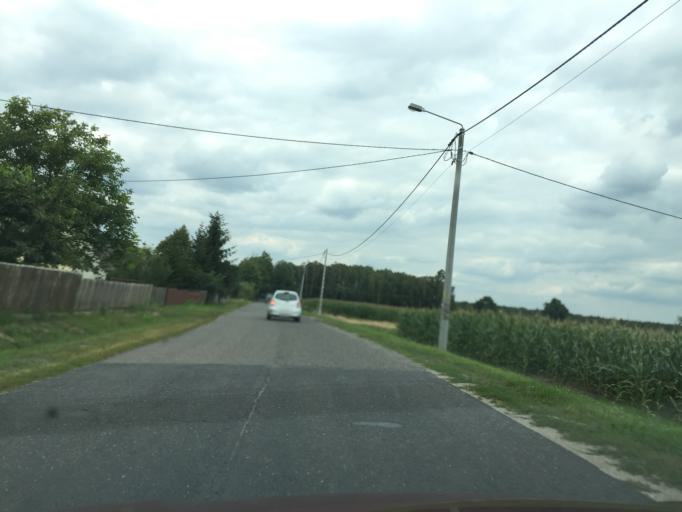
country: PL
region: Greater Poland Voivodeship
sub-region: Powiat kaliski
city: Stawiszyn
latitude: 51.9581
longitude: 18.1758
